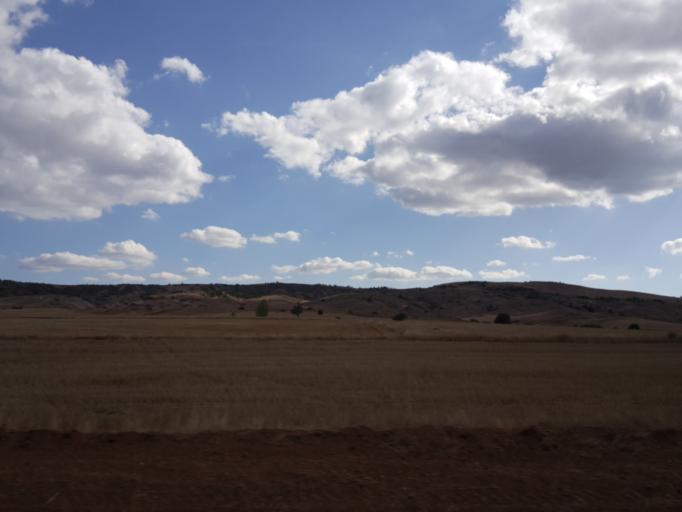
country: TR
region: Tokat
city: Sulusaray
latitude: 39.9866
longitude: 35.9649
